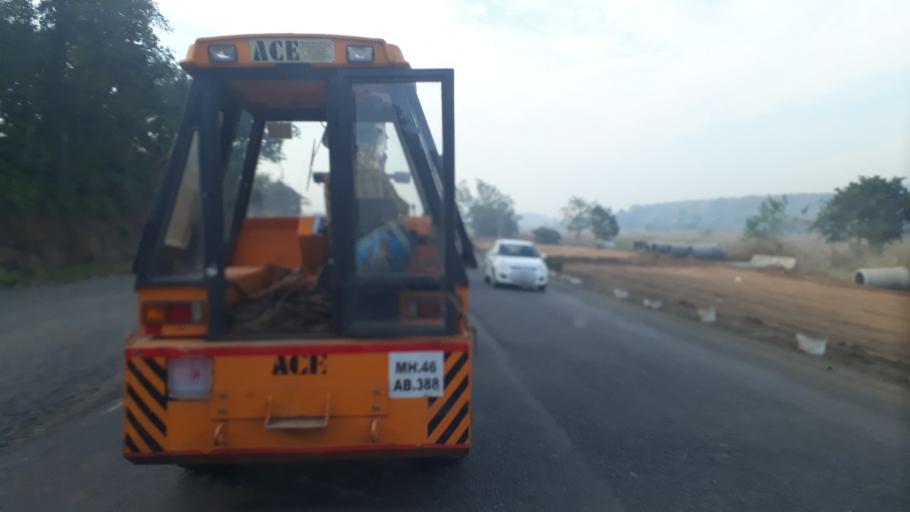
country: IN
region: Maharashtra
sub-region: Raigarh
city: Pen
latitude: 18.8526
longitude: 73.0968
